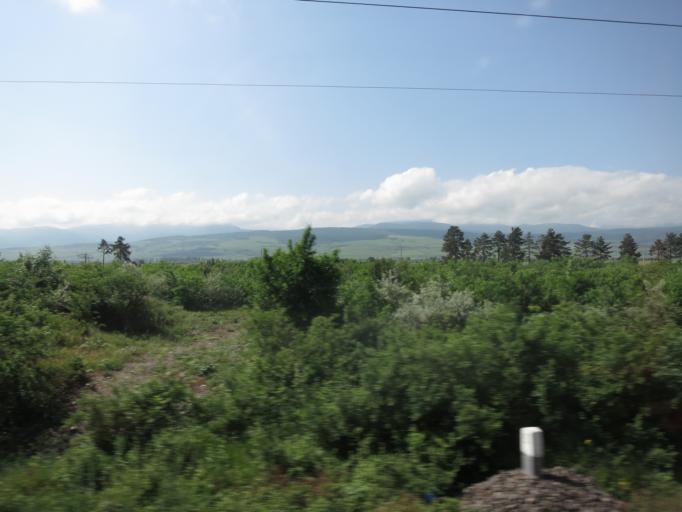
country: GE
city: Agara
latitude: 42.0287
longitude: 43.7679
